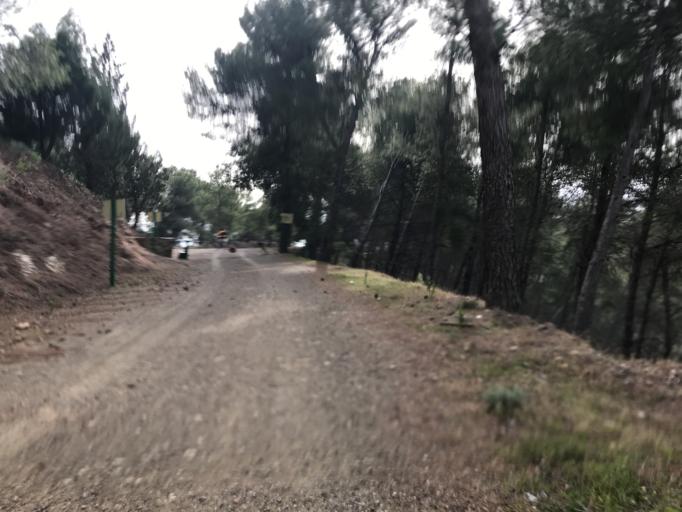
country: ES
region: Andalusia
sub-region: Provincia de Malaga
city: Malaga
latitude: 36.8000
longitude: -4.3993
